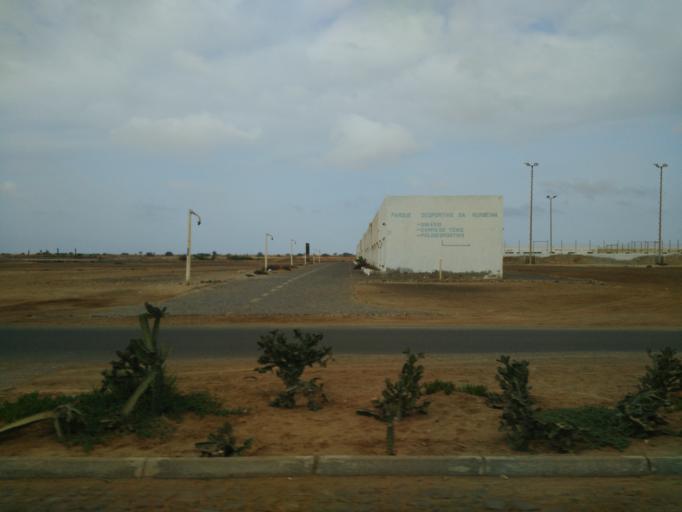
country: CV
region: Sal
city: Espargos
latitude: 16.6779
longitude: -22.9352
